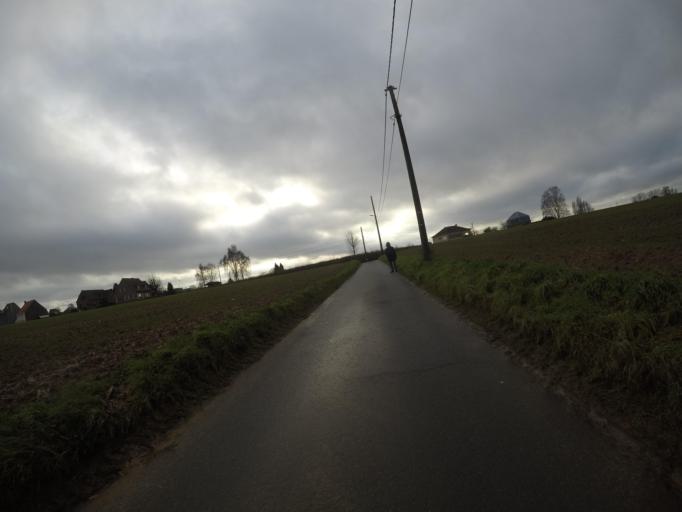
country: BE
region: Flanders
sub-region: Provincie Vlaams-Brabant
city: Gooik
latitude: 50.8022
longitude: 4.1234
